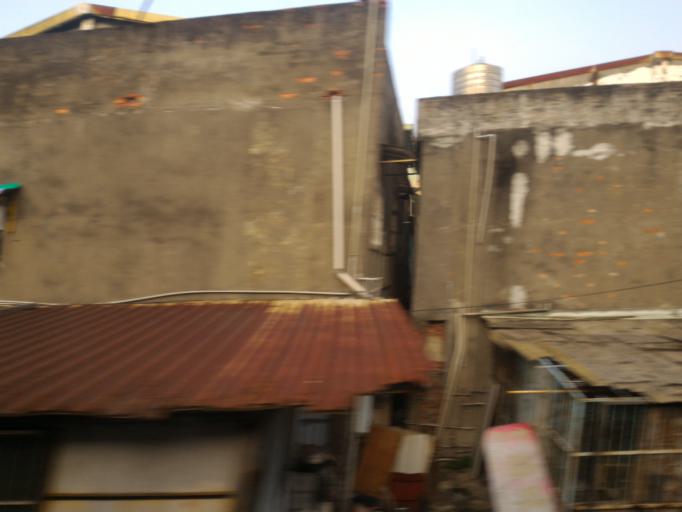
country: TW
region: Taiwan
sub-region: Taoyuan
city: Taoyuan
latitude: 24.9793
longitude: 121.3299
